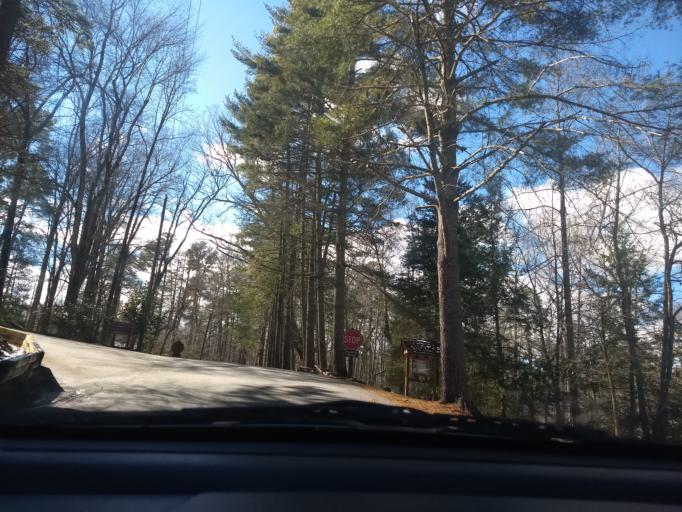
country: US
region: South Carolina
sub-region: Greenville County
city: Wade Hampton
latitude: 34.9268
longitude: -82.3689
